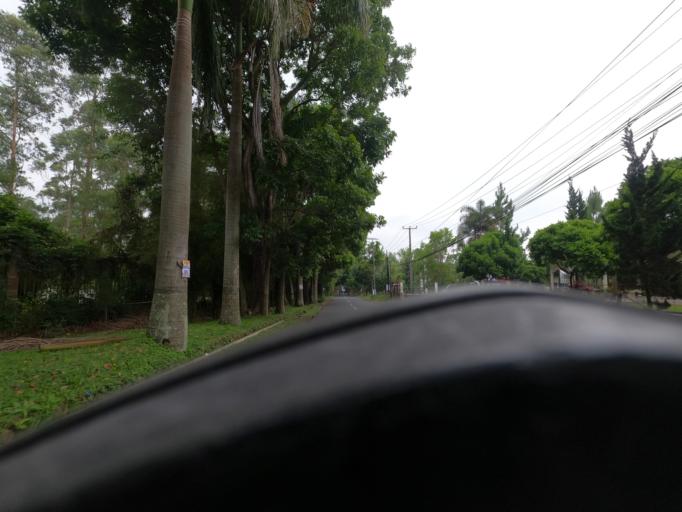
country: ID
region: West Java
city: Lembang
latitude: -6.8003
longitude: 107.5721
